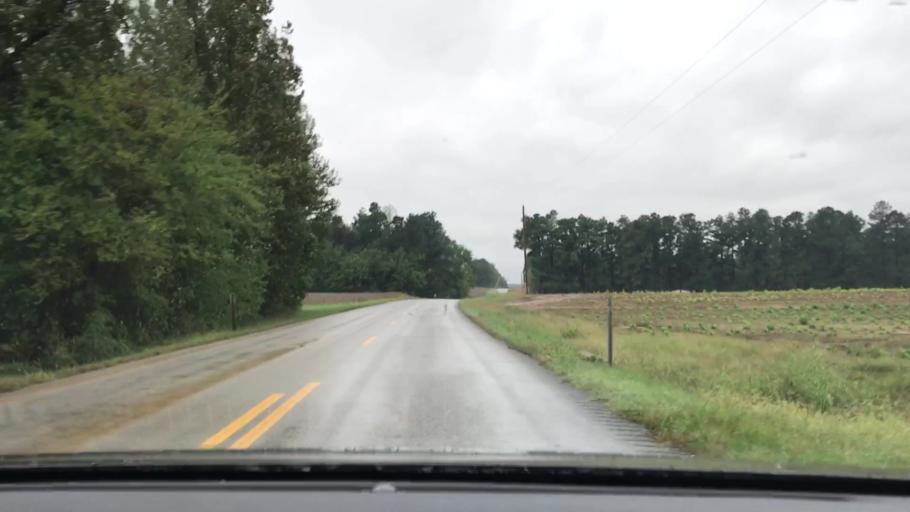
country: US
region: Kentucky
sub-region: McLean County
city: Calhoun
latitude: 37.4012
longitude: -87.2694
